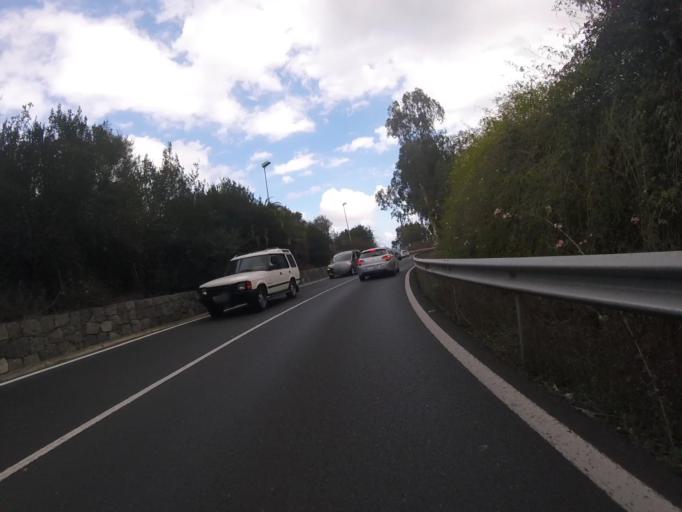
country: ES
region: Canary Islands
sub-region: Provincia de Las Palmas
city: Santa Brigida
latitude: 28.0236
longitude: -15.5136
